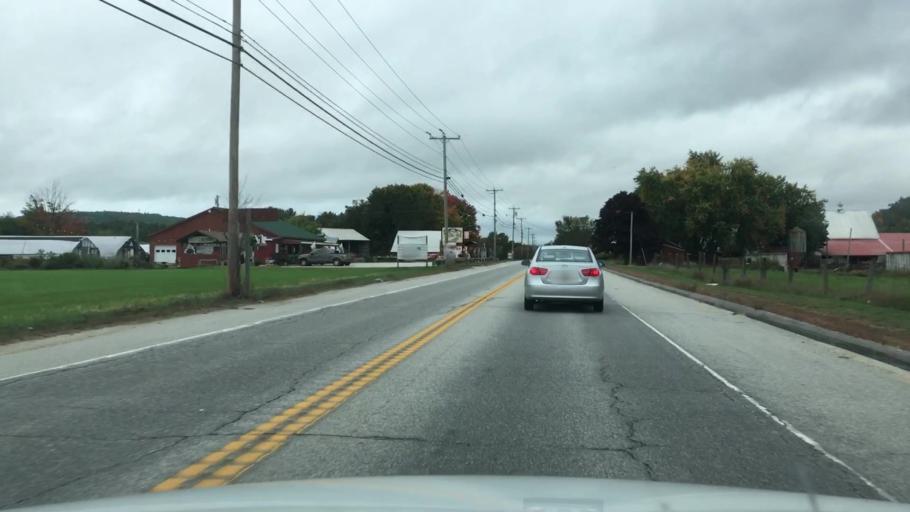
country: US
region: Maine
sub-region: Oxford County
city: South Paris
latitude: 44.1826
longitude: -70.5167
